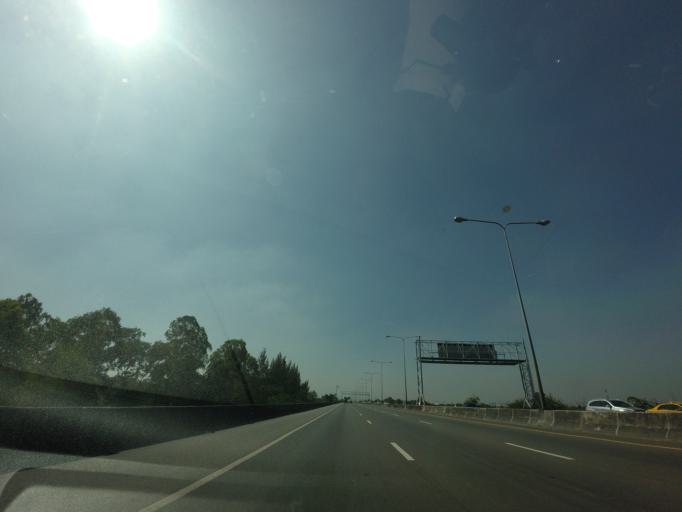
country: TH
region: Bangkok
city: Bang Na
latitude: 13.6304
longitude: 100.6719
